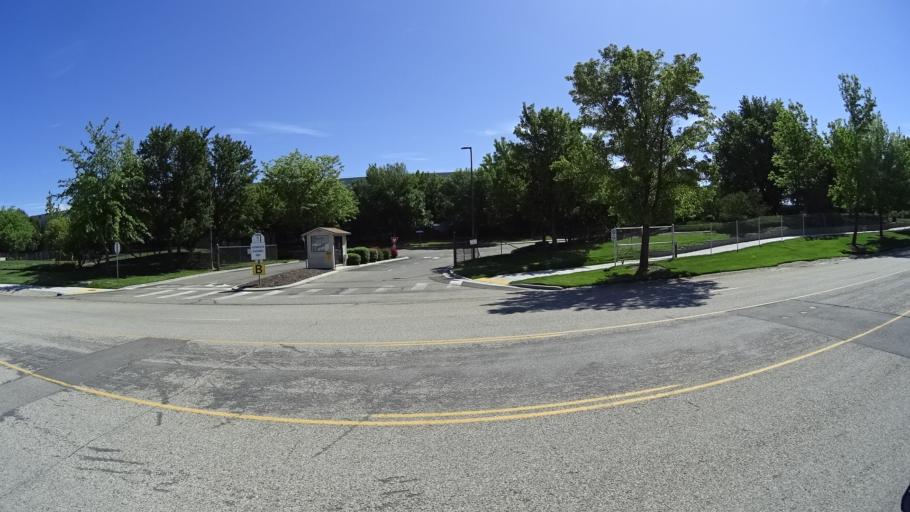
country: US
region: Idaho
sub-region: Ada County
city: Boise
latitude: 43.5258
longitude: -116.1491
